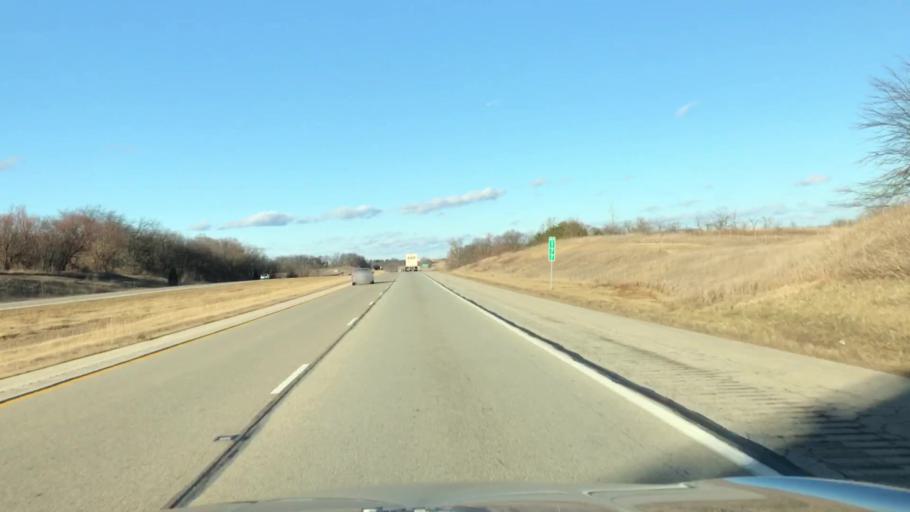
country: US
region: Illinois
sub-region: McLean County
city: Lexington
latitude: 40.6260
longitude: -88.8172
